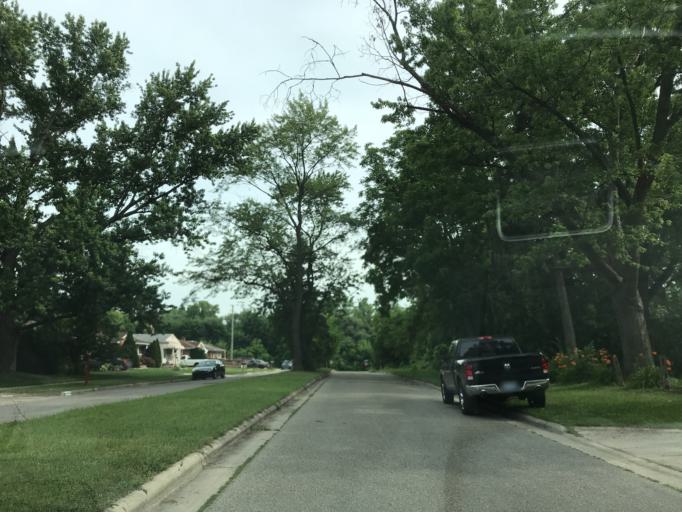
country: US
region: Michigan
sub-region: Wayne County
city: Redford
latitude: 42.4292
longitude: -83.3188
